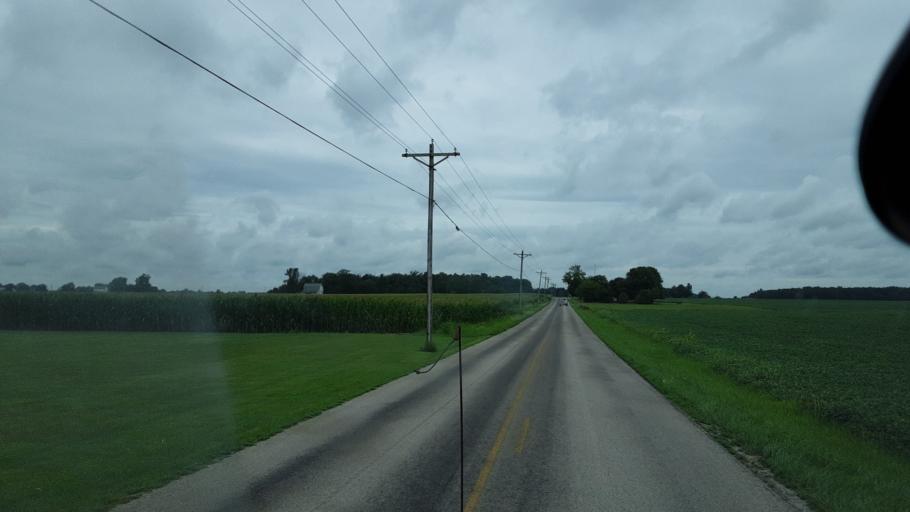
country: US
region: Indiana
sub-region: Jay County
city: Portland
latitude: 40.4795
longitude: -85.0207
